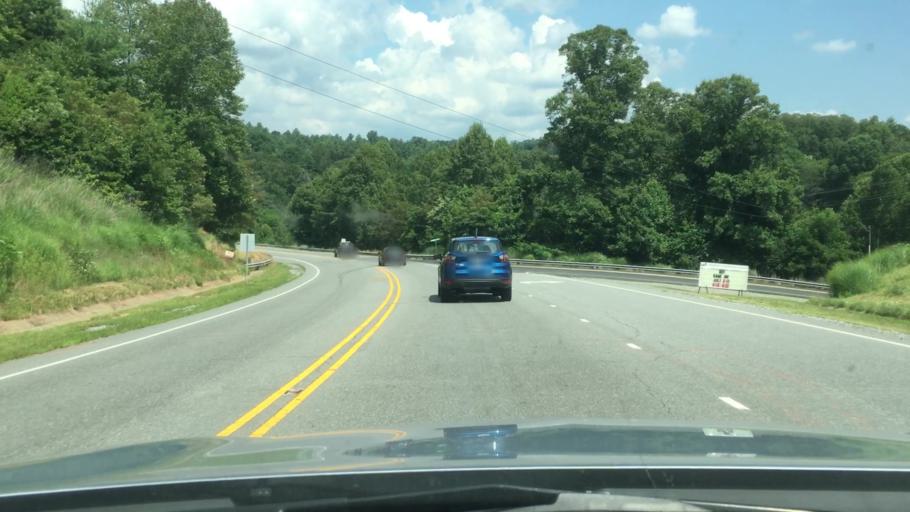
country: US
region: North Carolina
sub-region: Madison County
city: Mars Hill
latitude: 35.8243
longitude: -82.5646
